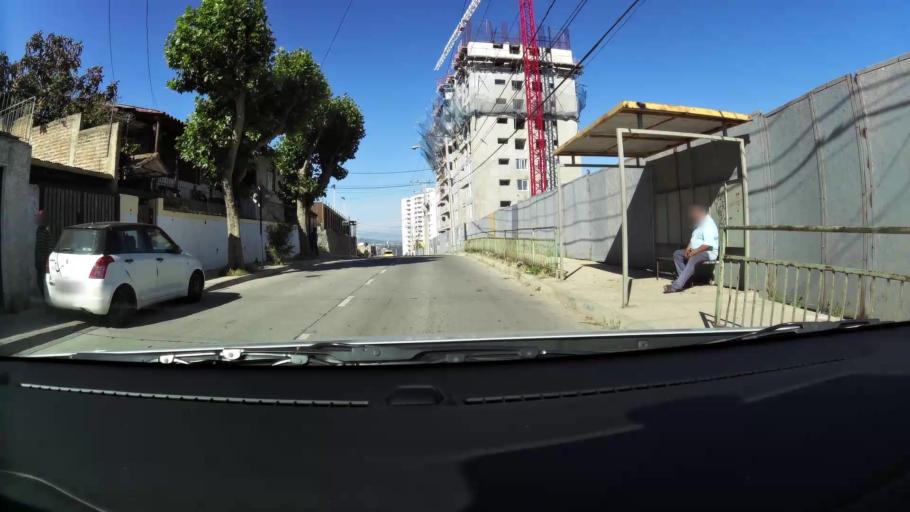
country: CL
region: Valparaiso
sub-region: Provincia de Valparaiso
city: Vina del Mar
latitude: -33.0443
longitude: -71.5581
